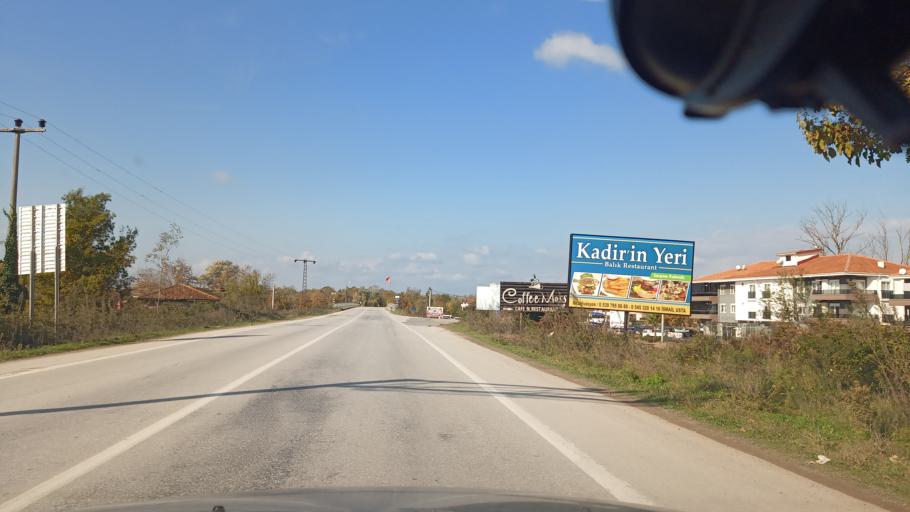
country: TR
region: Sakarya
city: Karasu
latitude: 41.1182
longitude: 30.6480
